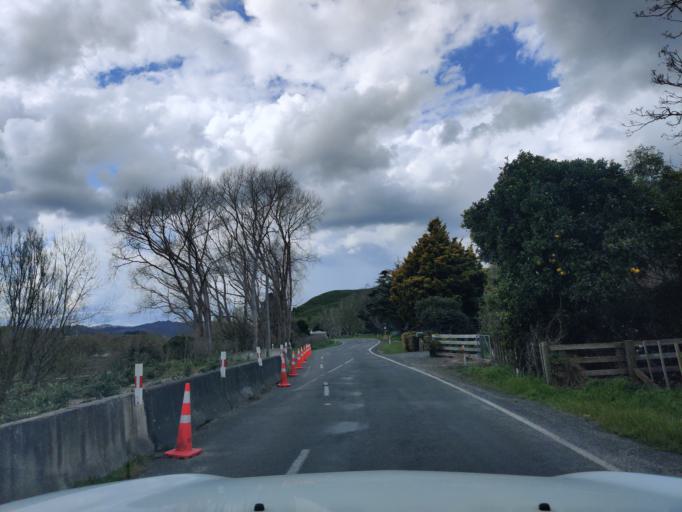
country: NZ
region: Manawatu-Wanganui
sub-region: Wanganui District
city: Wanganui
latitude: -39.8759
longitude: 175.1108
